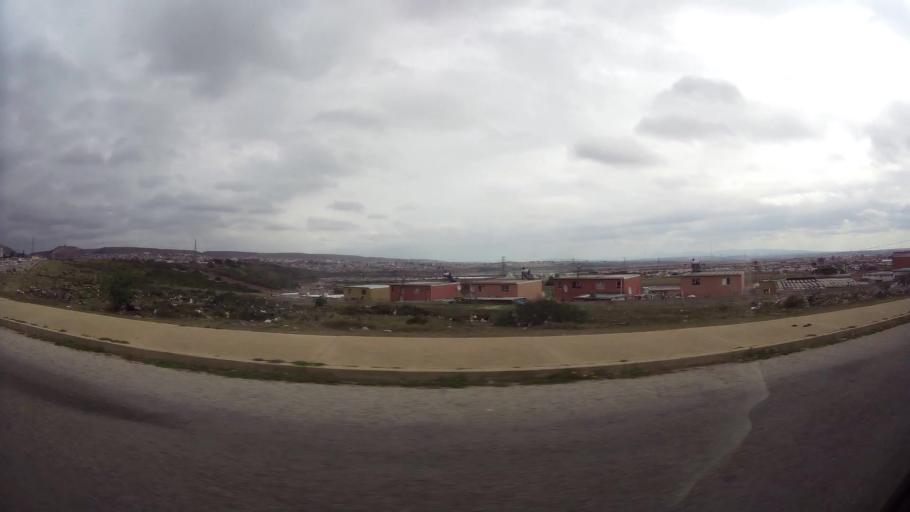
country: ZA
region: Eastern Cape
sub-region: Nelson Mandela Bay Metropolitan Municipality
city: Port Elizabeth
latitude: -33.8921
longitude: 25.5563
